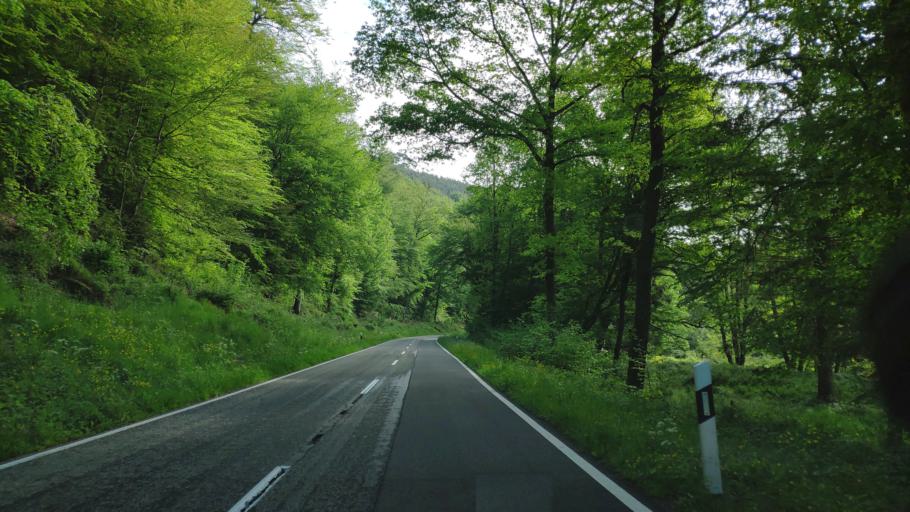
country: DE
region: Rheinland-Pfalz
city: Hinterweidenthal
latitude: 49.1917
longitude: 7.7284
